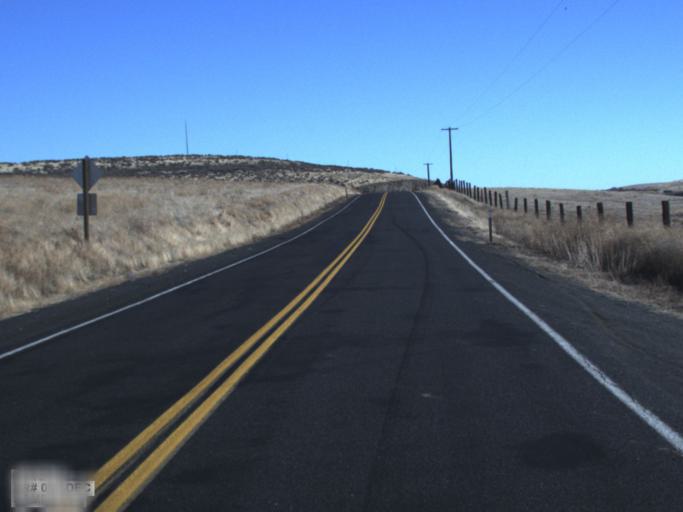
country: US
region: Washington
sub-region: Adams County
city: Ritzville
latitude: 46.9710
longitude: -118.6560
